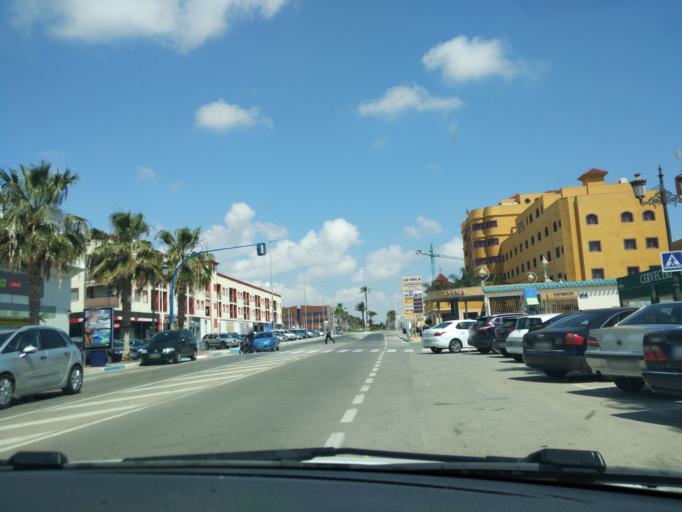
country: ES
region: Murcia
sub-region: Murcia
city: Los Alcazares
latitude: 37.7486
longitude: -0.8480
